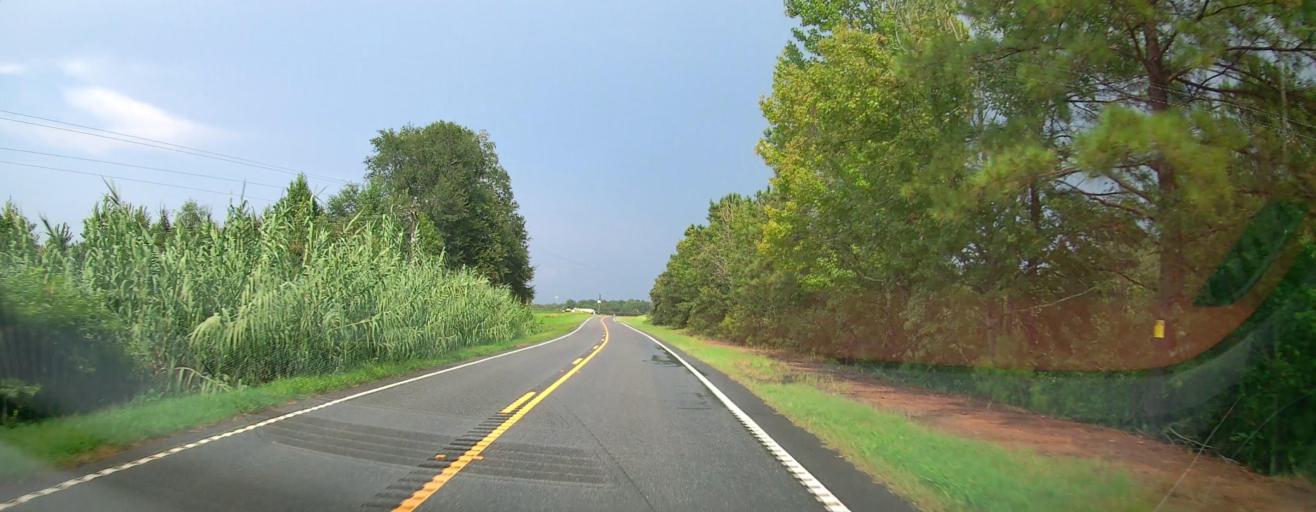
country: US
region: Georgia
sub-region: Twiggs County
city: Jeffersonville
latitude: 32.5944
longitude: -83.3399
